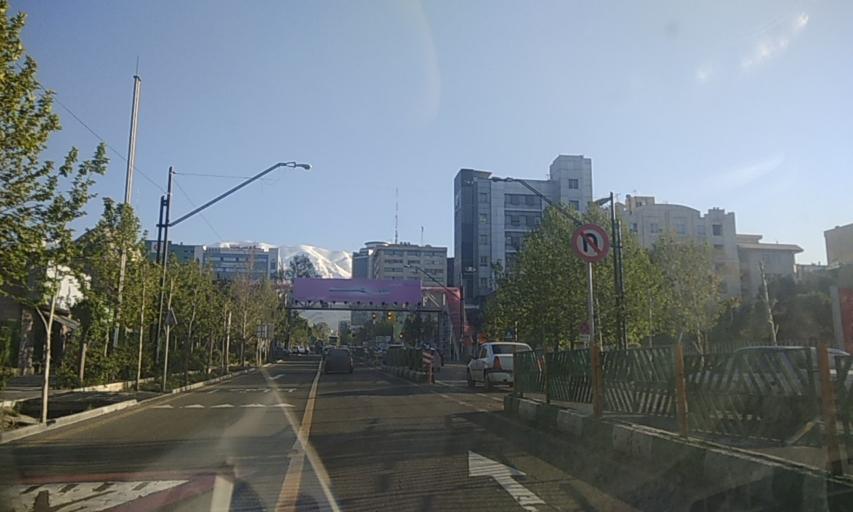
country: IR
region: Tehran
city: Tajrish
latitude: 35.7654
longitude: 51.4107
